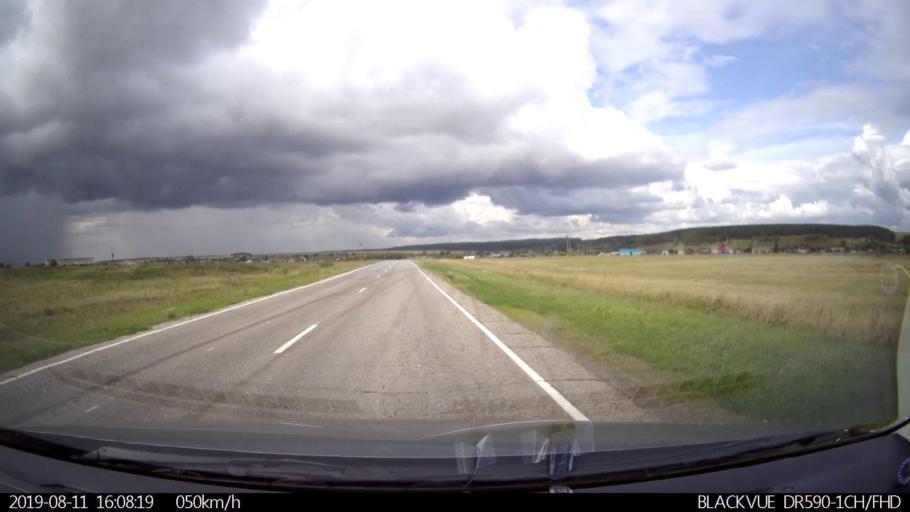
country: RU
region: Ulyanovsk
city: Ignatovka
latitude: 53.9835
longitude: 47.6482
